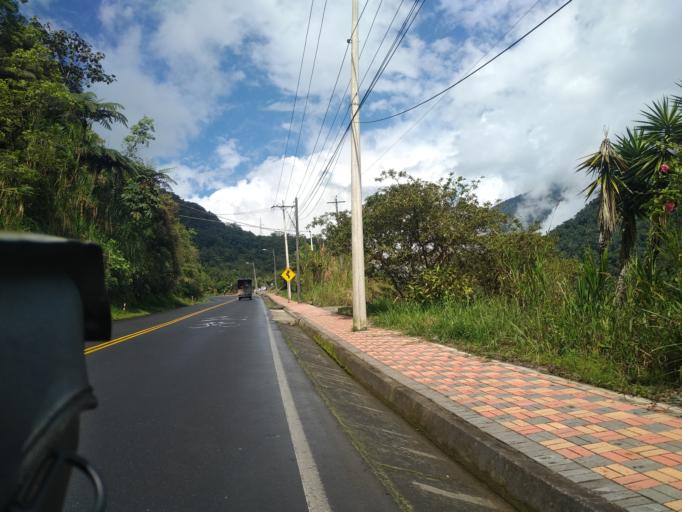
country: EC
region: Tungurahua
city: Banos
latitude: -1.4018
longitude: -78.2851
